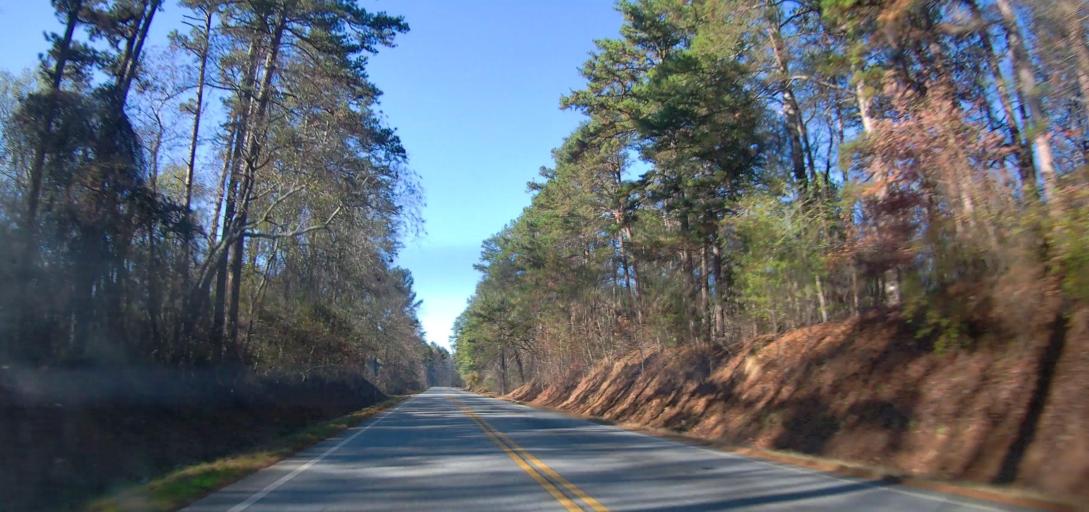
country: US
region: Georgia
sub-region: Hall County
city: Lula
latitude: 34.4204
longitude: -83.7084
